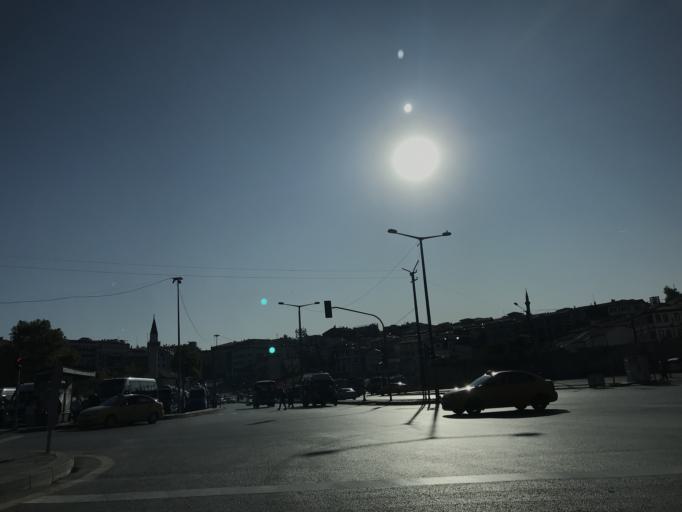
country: TR
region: Ankara
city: Ankara
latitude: 39.9436
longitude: 32.8616
